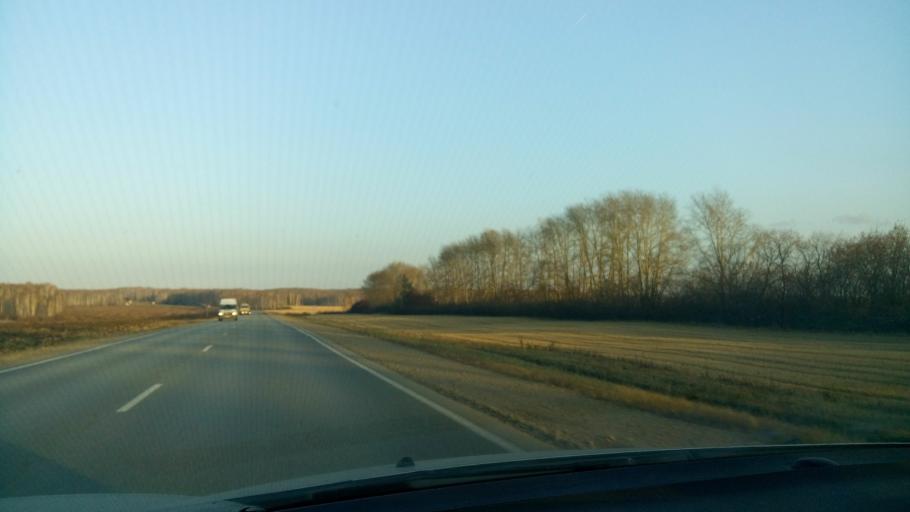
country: RU
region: Sverdlovsk
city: Yelanskiy
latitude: 56.7594
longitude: 62.3829
